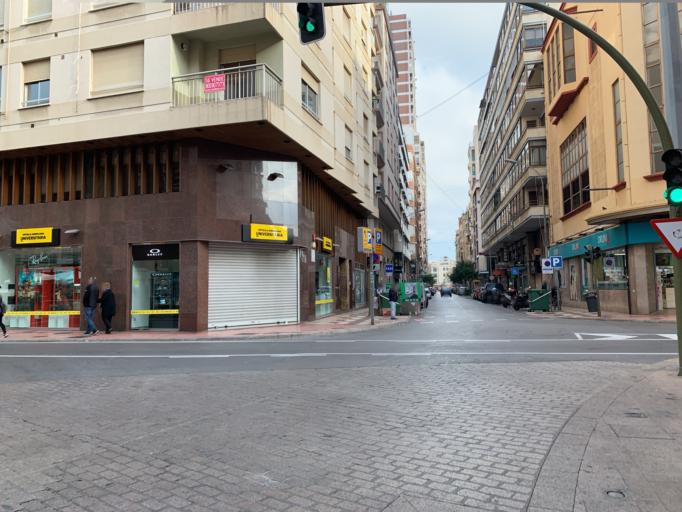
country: ES
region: Valencia
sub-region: Provincia de Castello
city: Castello de la Plana
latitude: 39.9836
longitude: -0.0382
